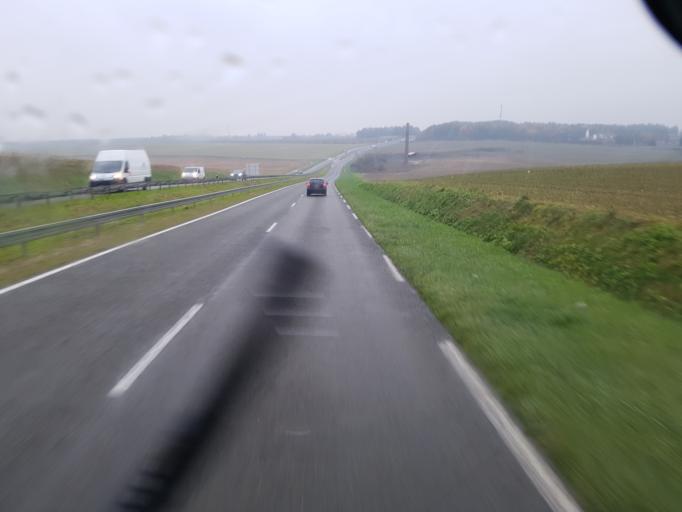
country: FR
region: Picardie
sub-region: Departement de l'Aisne
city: Gauchy
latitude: 49.8053
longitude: 3.2862
